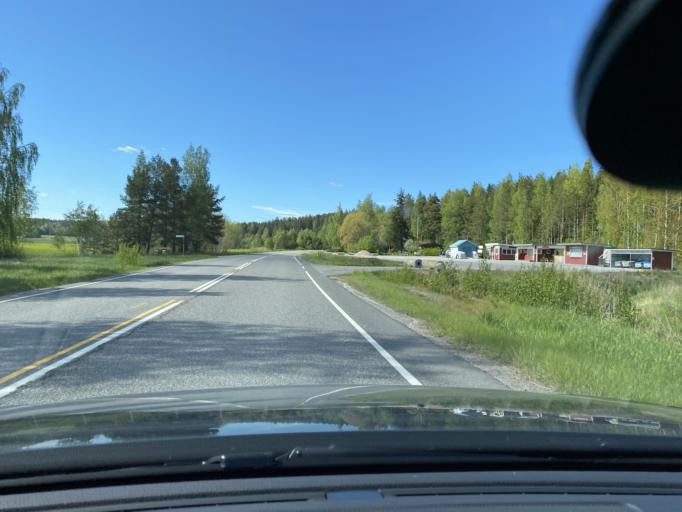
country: FI
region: Varsinais-Suomi
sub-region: Turku
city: Sauvo
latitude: 60.3695
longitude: 22.6727
